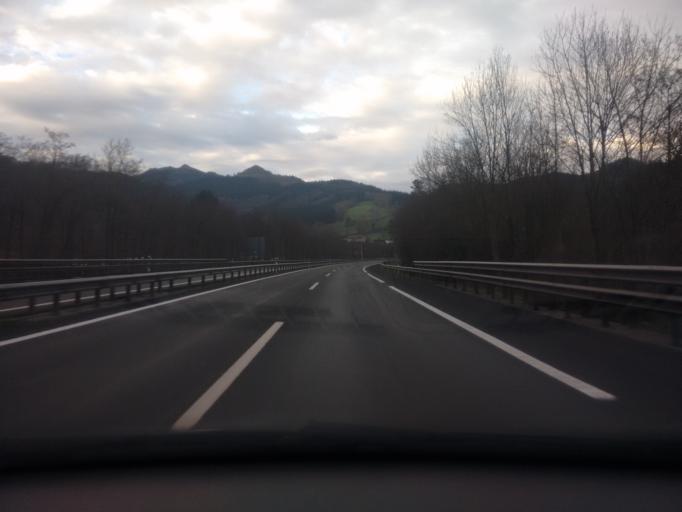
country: ES
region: Basque Country
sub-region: Provincia de Guipuzcoa
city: Cestona
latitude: 43.2612
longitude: -2.2810
